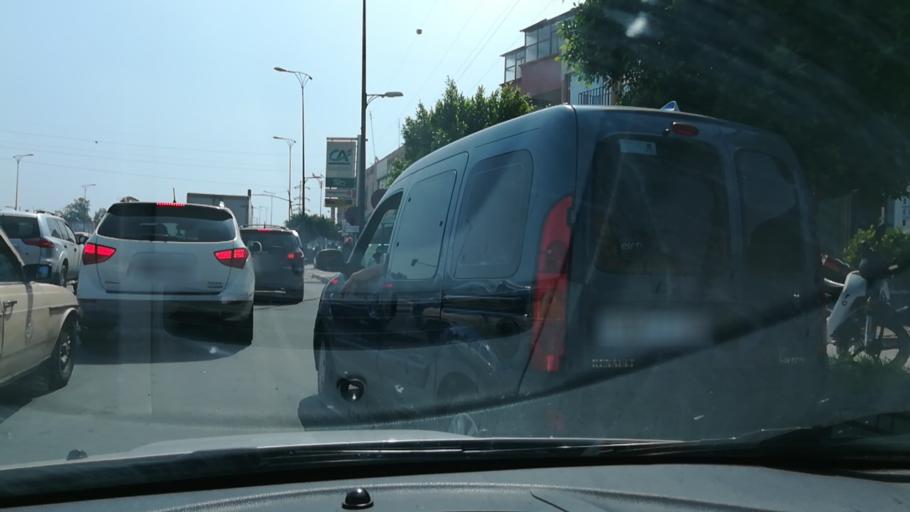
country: MA
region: Marrakech-Tensift-Al Haouz
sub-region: Marrakech
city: Marrakesh
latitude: 31.6273
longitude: -8.0387
